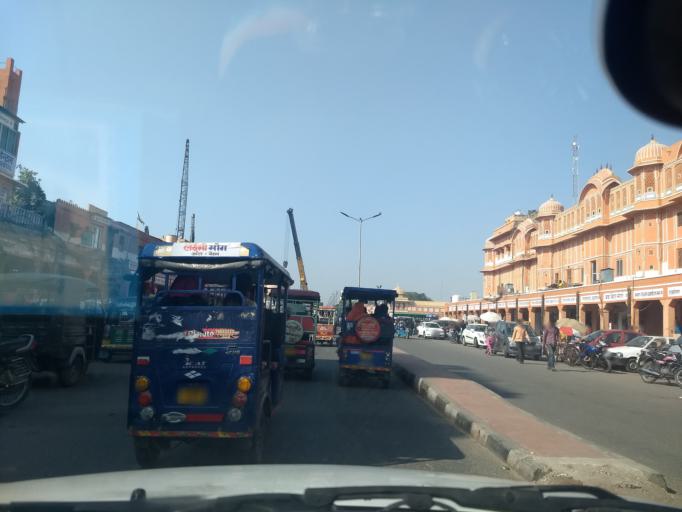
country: IN
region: Rajasthan
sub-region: Jaipur
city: Jaipur
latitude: 26.9226
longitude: 75.8281
